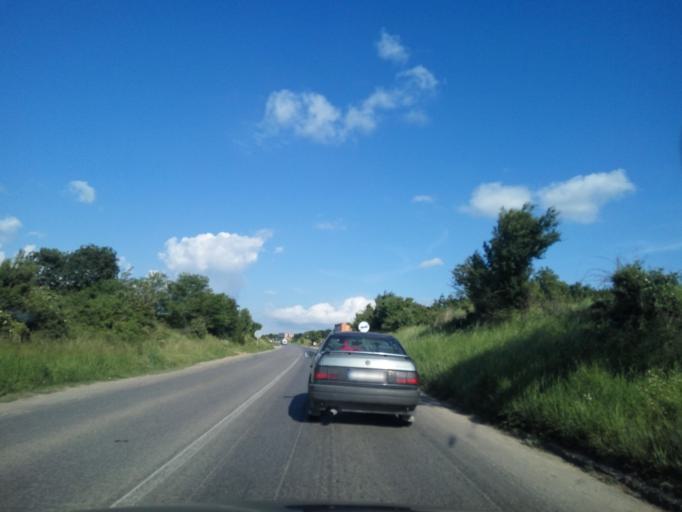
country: XK
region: Prizren
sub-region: Komuna e Malisheves
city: Llazice
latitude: 42.5879
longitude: 20.6723
